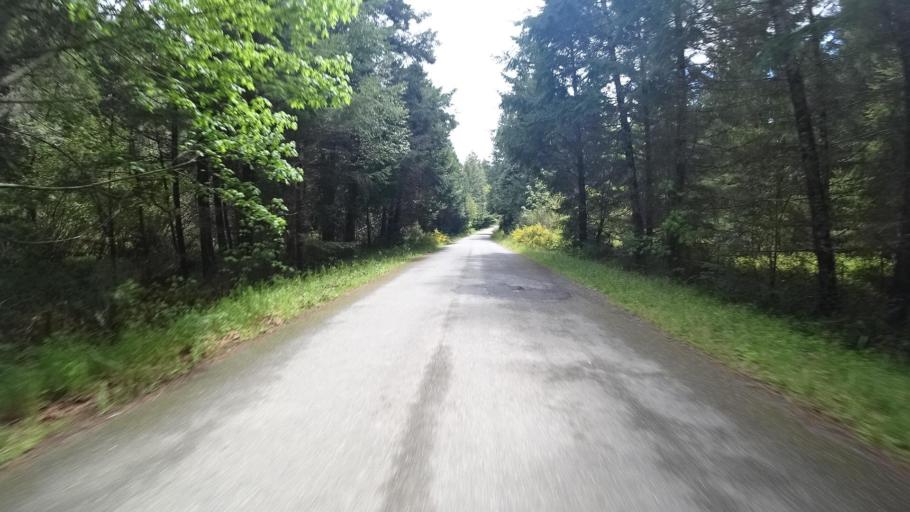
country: US
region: California
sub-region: Humboldt County
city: Blue Lake
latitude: 40.7765
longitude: -123.8771
